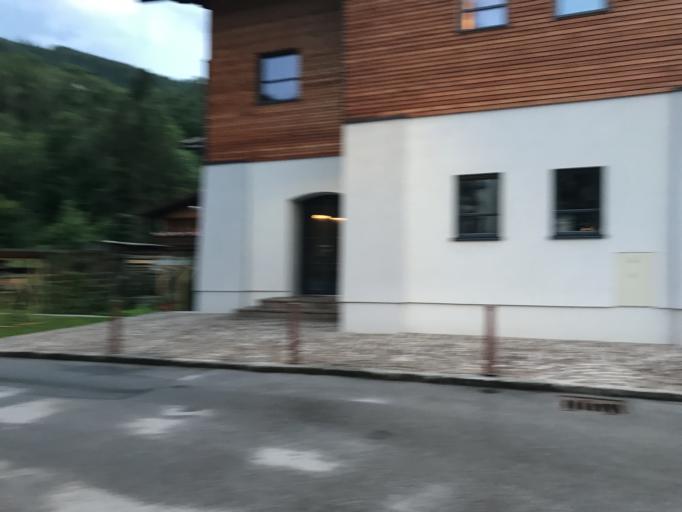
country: AT
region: Salzburg
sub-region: Politischer Bezirk Sankt Johann im Pongau
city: Wagrain
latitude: 47.3336
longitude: 13.2958
